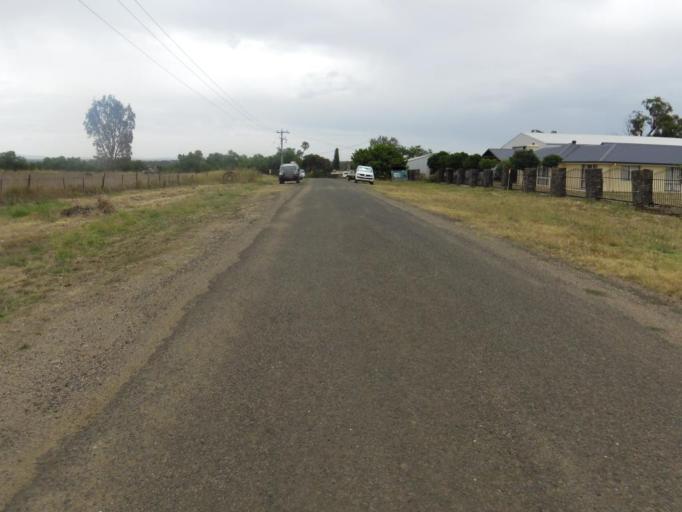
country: AU
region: Victoria
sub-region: Greater Bendigo
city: Epsom
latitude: -36.7893
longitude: 144.5141
